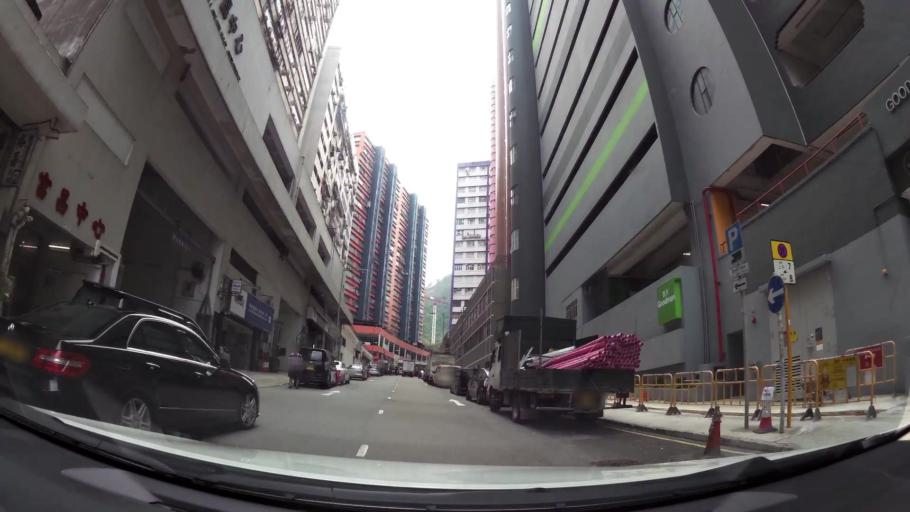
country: HK
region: Sha Tin
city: Sha Tin
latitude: 22.3973
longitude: 114.1909
